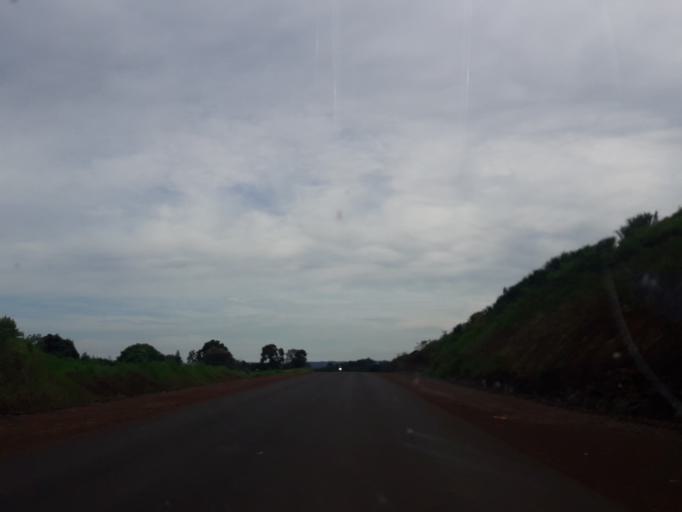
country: AR
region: Misiones
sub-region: Departamento de San Pedro
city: San Pedro
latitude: -26.5228
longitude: -53.9399
